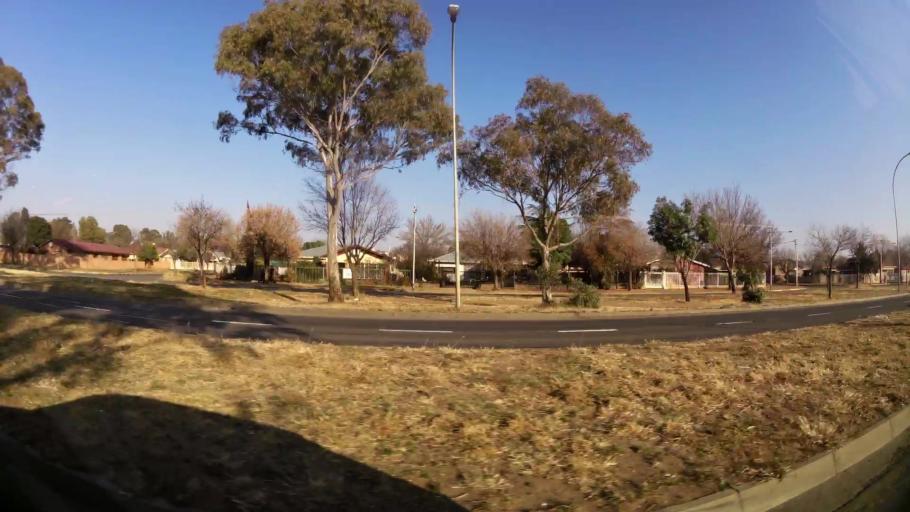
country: ZA
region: Orange Free State
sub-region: Mangaung Metropolitan Municipality
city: Bloemfontein
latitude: -29.1504
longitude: 26.2172
